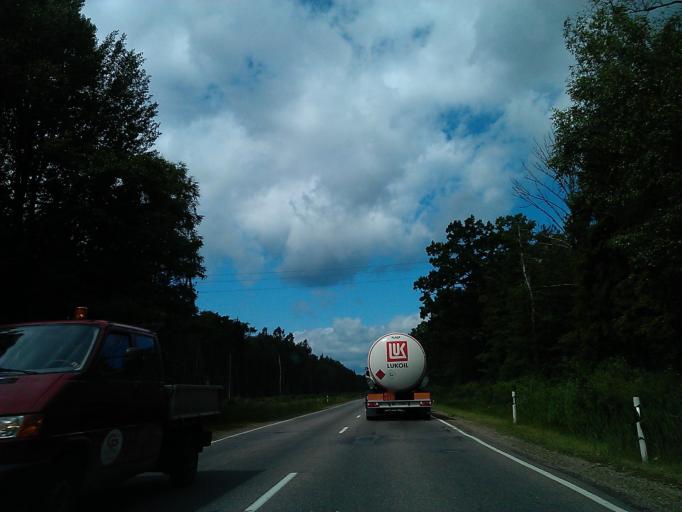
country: LV
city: Tireli
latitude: 56.9312
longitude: 23.5022
